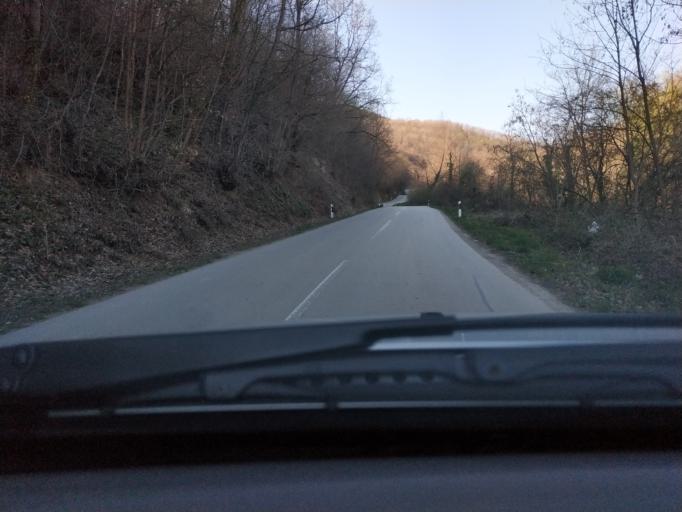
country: RS
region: Central Serbia
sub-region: Nisavski Okrug
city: Aleksinac
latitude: 43.5380
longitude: 21.8037
